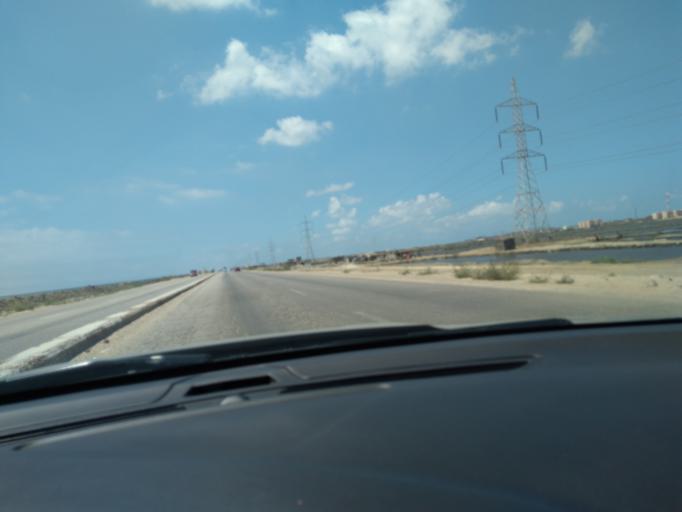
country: EG
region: Muhafazat ad Daqahliyah
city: Al Matariyah
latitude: 31.3177
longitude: 32.1155
